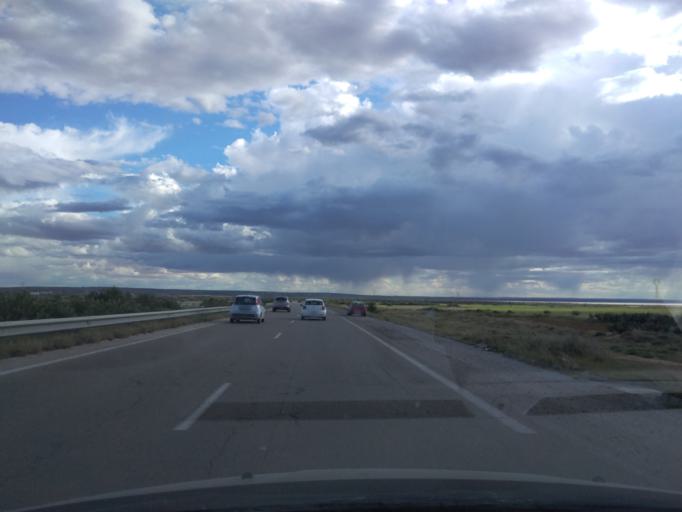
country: TN
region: Al Munastir
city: Manzil Kamil
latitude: 35.5056
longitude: 10.6254
